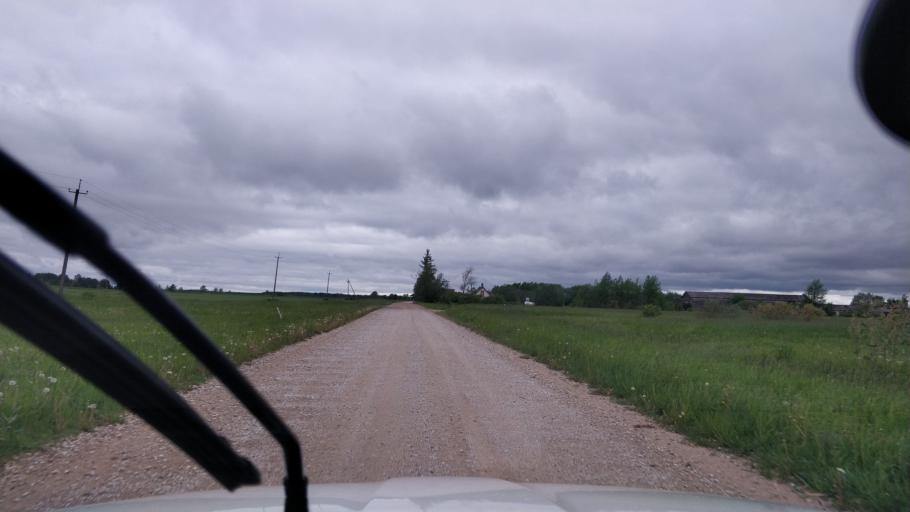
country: EE
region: Raplamaa
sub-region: Maerjamaa vald
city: Marjamaa
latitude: 58.7149
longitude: 24.2402
